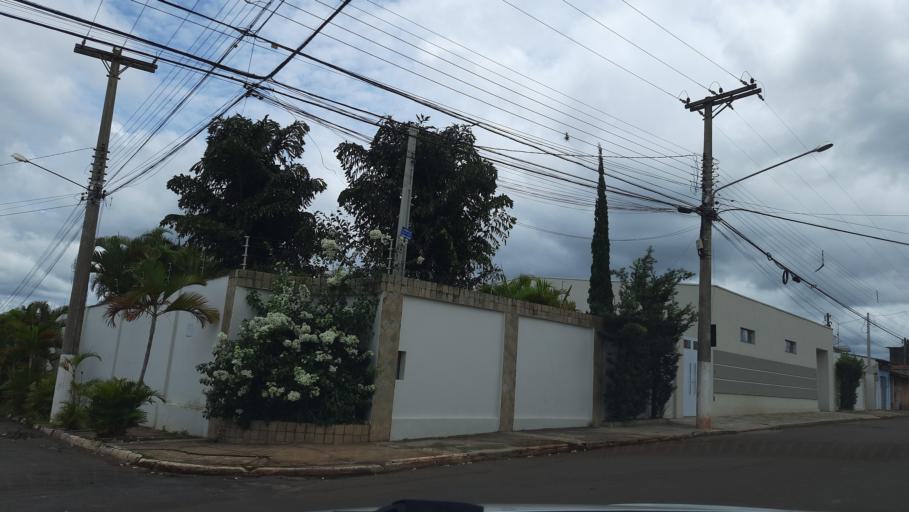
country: BR
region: Sao Paulo
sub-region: Casa Branca
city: Casa Branca
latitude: -21.7819
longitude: -47.0953
